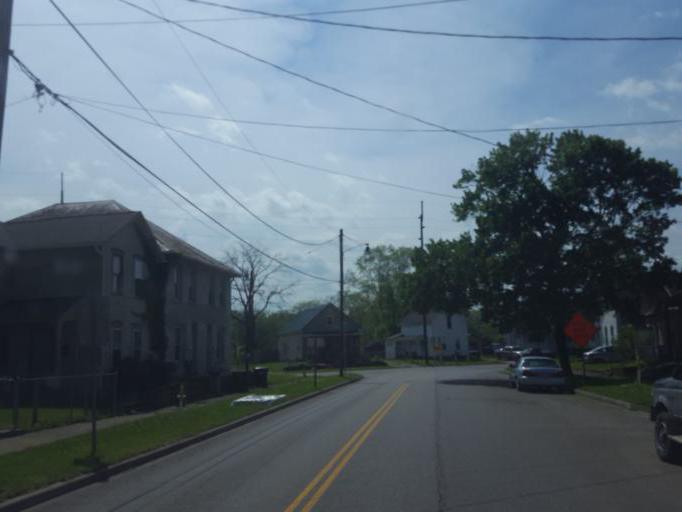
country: US
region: Ohio
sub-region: Licking County
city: Newark
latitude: 40.0510
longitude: -82.4014
